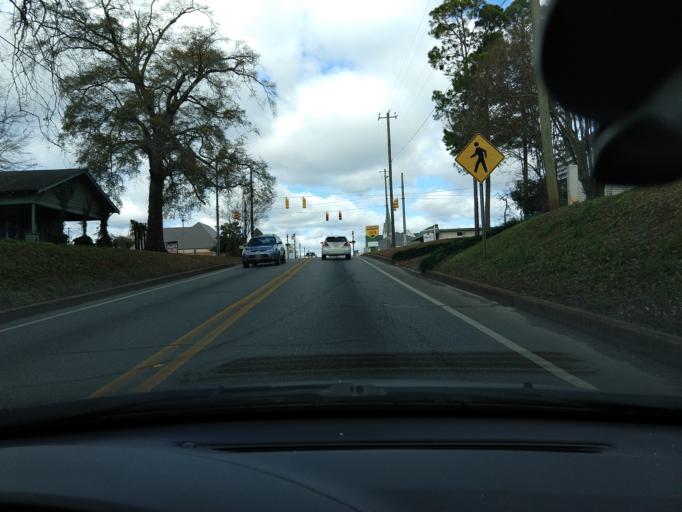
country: US
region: Alabama
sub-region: Coffee County
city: Enterprise
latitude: 31.3111
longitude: -85.8512
